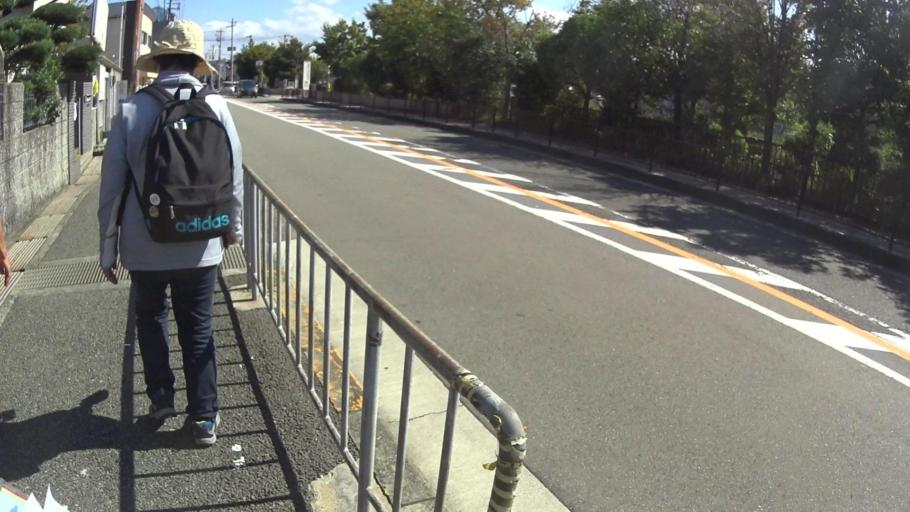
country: JP
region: Ehime
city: Kihoku-cho
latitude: 33.3819
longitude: 132.8240
